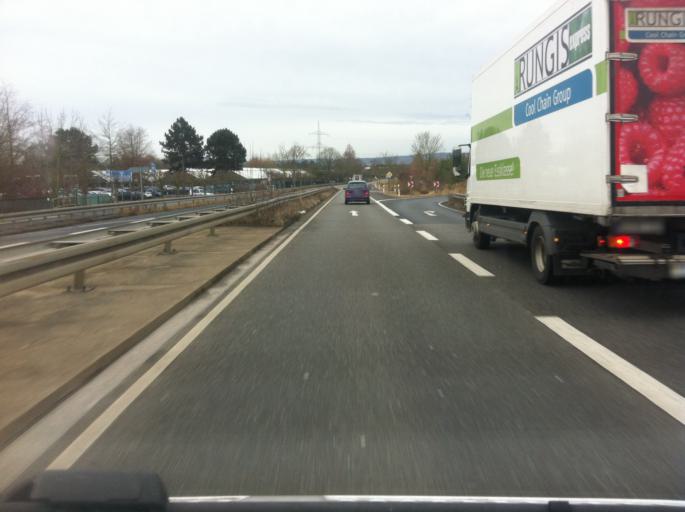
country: DE
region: North Rhine-Westphalia
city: Meckenheim
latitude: 50.6402
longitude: 7.0361
